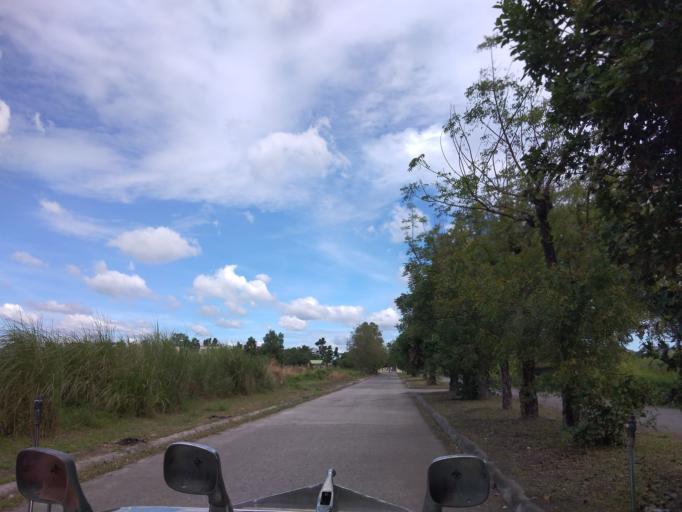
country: PH
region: Central Luzon
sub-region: Province of Pampanga
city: Pandacaqui
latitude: 15.1750
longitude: 120.6545
